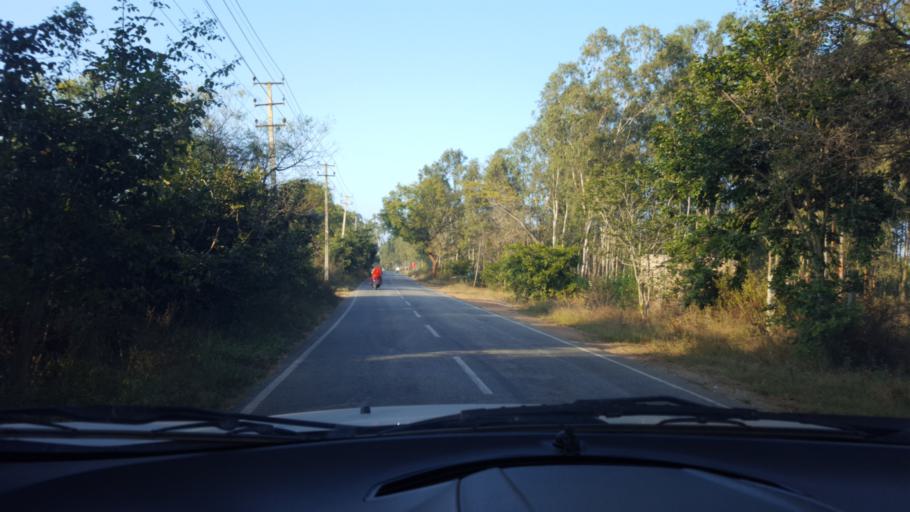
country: IN
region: Karnataka
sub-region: Bangalore Urban
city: Yelahanka
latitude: 13.1786
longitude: 77.5993
